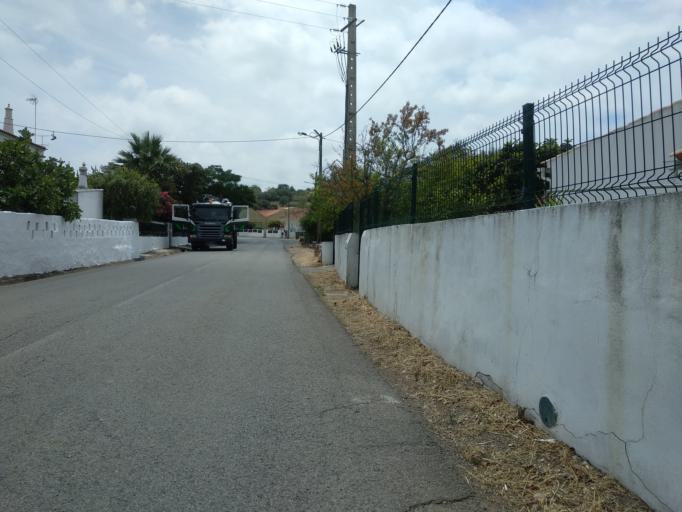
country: PT
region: Faro
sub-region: Sao Bras de Alportel
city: Sao Bras de Alportel
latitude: 37.1665
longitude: -7.8918
